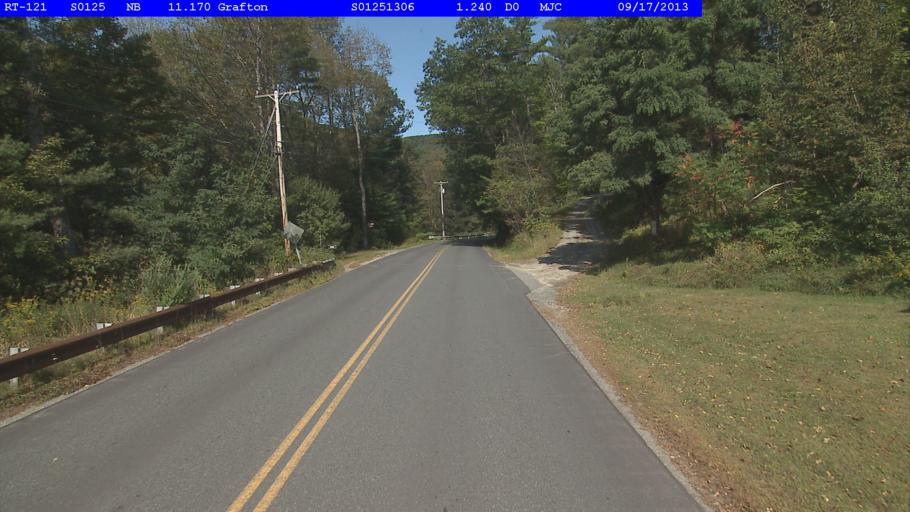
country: US
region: Vermont
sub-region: Windham County
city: Rockingham
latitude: 43.1575
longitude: -72.5759
